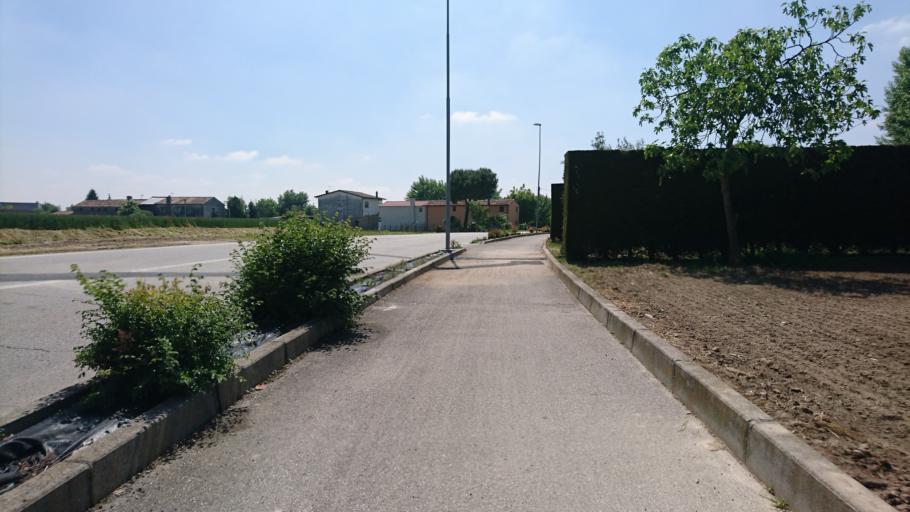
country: IT
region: Veneto
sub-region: Provincia di Padova
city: Casalserugo
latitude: 45.3140
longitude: 11.9089
